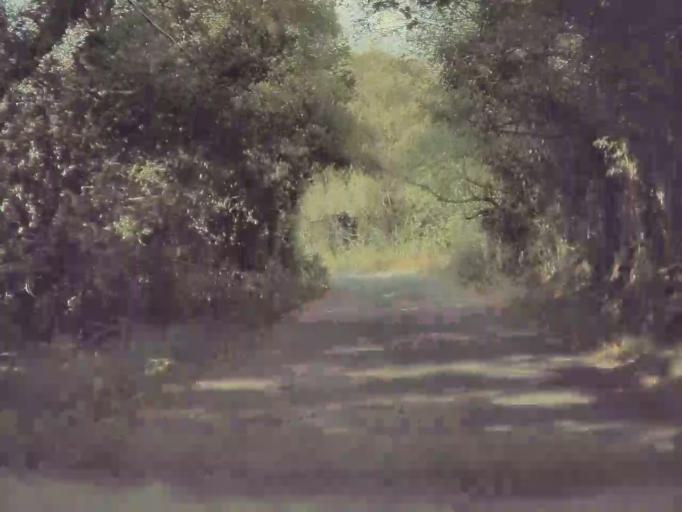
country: IE
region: Leinster
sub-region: Wicklow
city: Rathdrum
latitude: 53.0272
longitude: -6.3078
